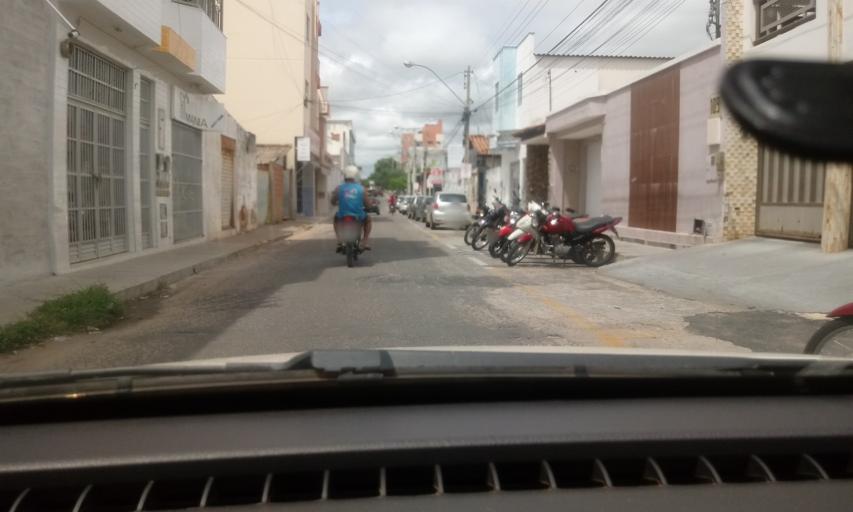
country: BR
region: Bahia
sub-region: Guanambi
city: Guanambi
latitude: -14.2244
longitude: -42.7787
